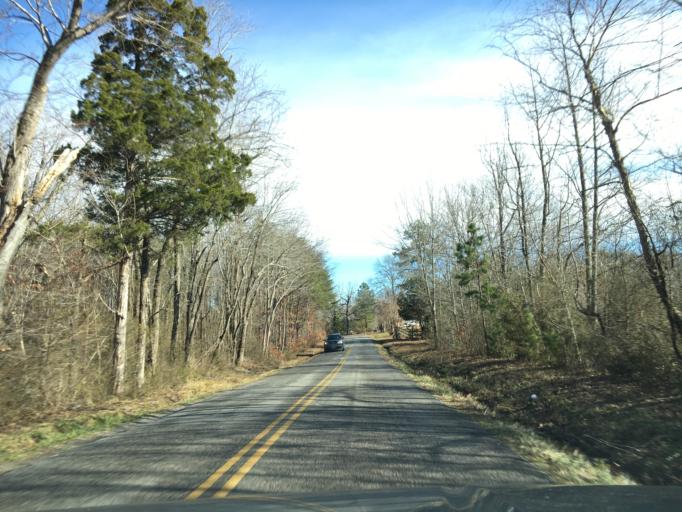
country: US
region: Virginia
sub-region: Amelia County
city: Amelia Court House
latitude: 37.3978
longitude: -78.0947
